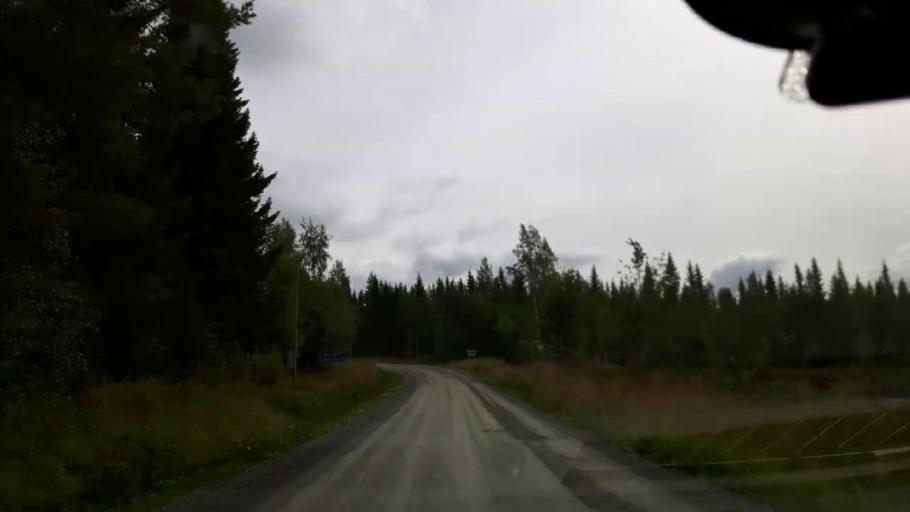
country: SE
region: Jaemtland
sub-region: Krokoms Kommun
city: Valla
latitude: 63.6412
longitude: 13.9979
